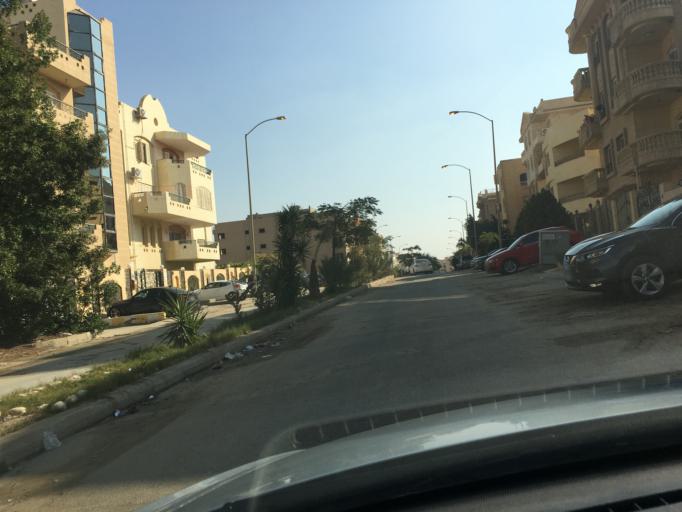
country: EG
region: Al Jizah
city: Madinat Sittah Uktubar
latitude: 29.9988
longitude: 30.9875
